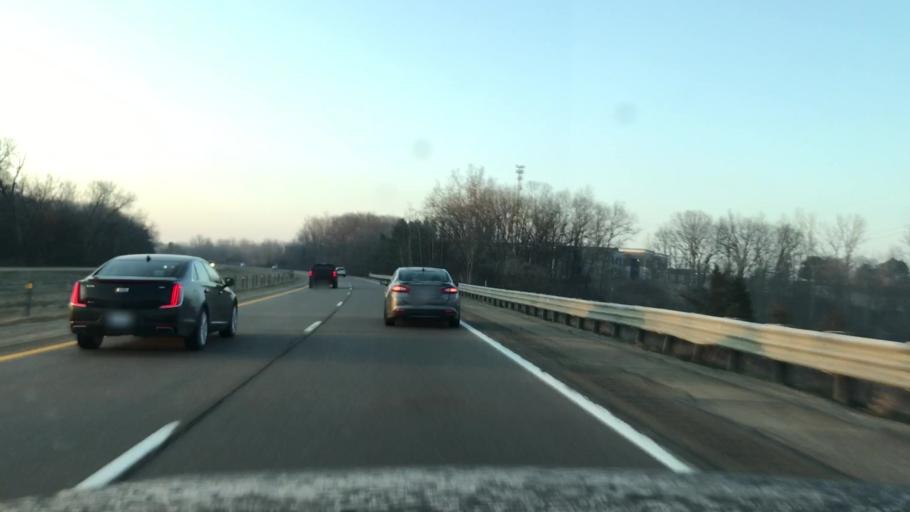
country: US
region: Michigan
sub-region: Kent County
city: East Grand Rapids
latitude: 42.9363
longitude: -85.5661
